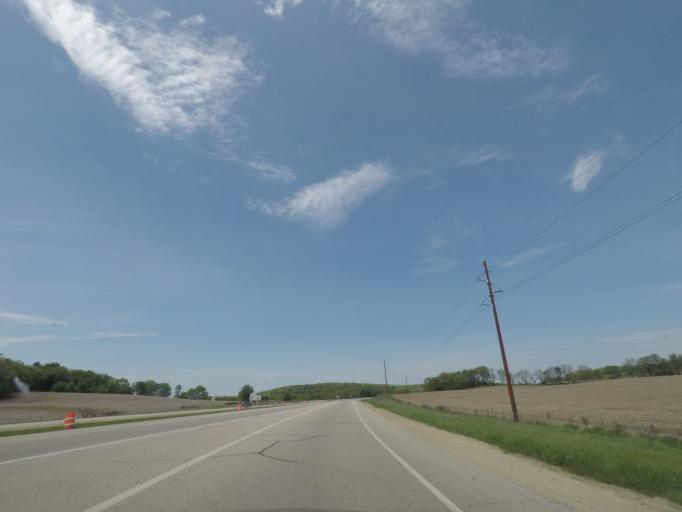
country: US
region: Wisconsin
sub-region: Dane County
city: Oregon
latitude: 42.9539
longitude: -89.3810
